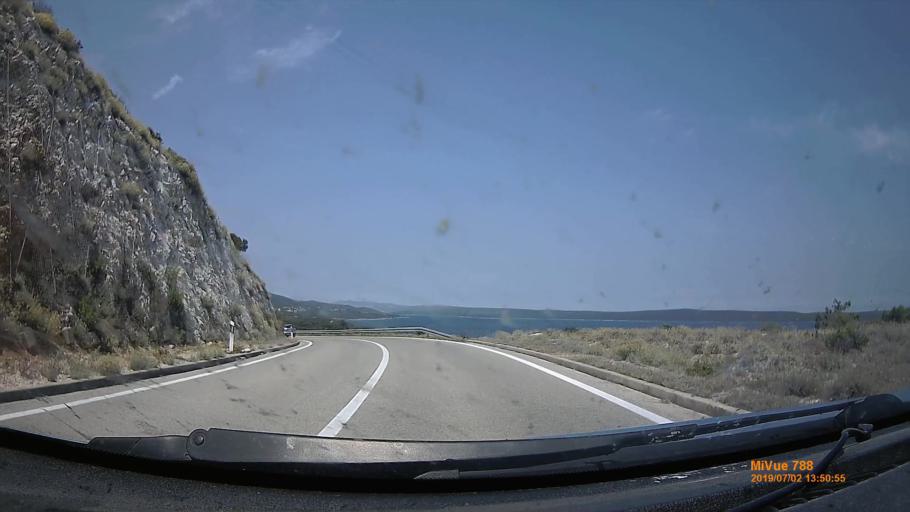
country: HR
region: Primorsko-Goranska
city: Mali Losinj
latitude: 44.6004
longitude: 14.4066
